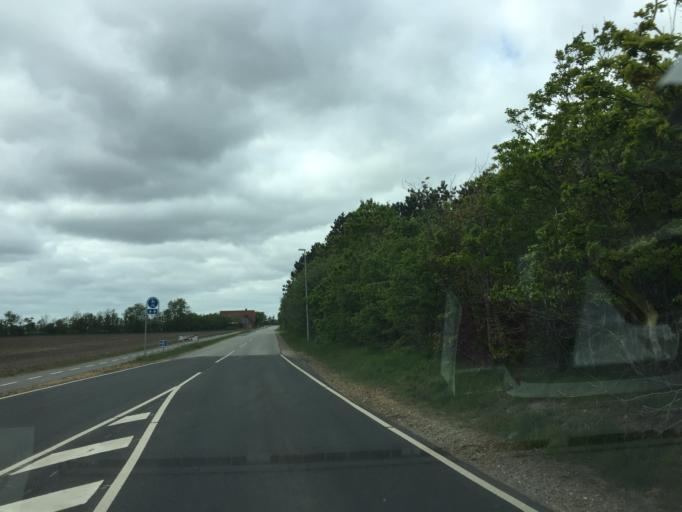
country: DK
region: Central Jutland
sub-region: Ringkobing-Skjern Kommune
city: Skjern
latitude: 55.9709
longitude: 8.3620
